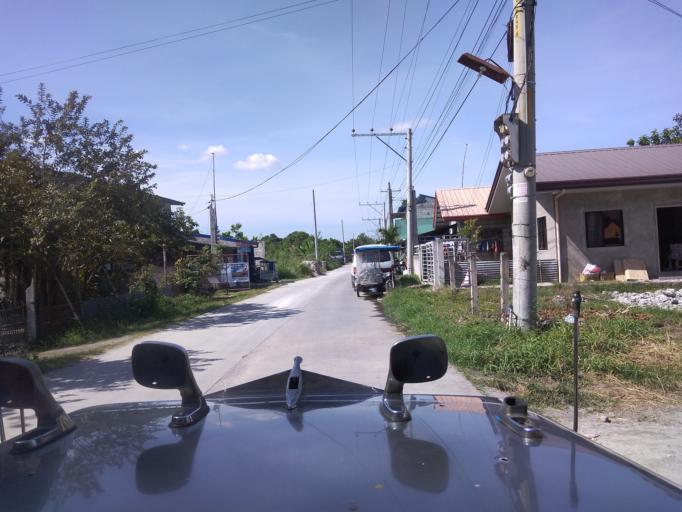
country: PH
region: Central Luzon
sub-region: Province of Pampanga
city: Magliman
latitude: 15.0206
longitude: 120.6557
